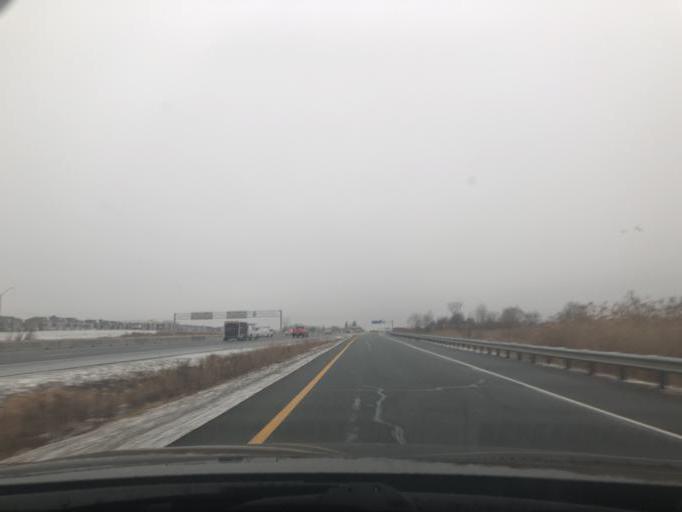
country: CA
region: Ontario
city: Markham
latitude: 43.8744
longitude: -79.2169
